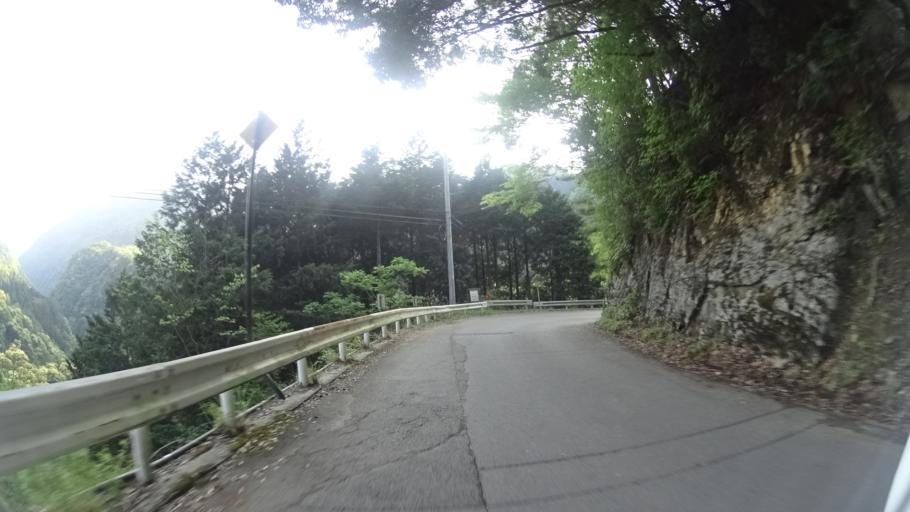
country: JP
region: Tokushima
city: Ikedacho
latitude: 33.9462
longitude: 133.8182
